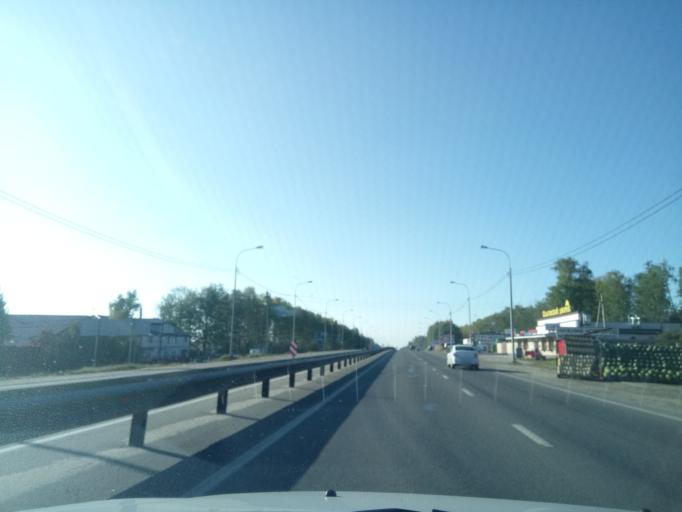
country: RU
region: Nizjnij Novgorod
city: Nizhniy Novgorod
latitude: 56.2135
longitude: 43.9294
